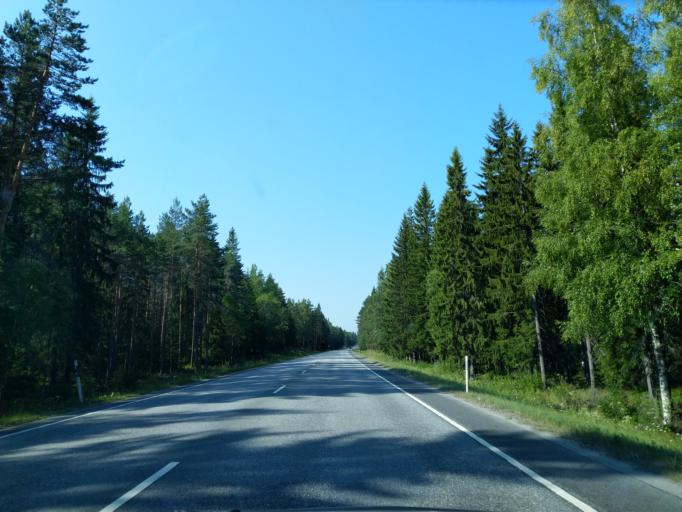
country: FI
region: Satakunta
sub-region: Pori
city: Noormarkku
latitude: 61.6271
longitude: 21.9230
